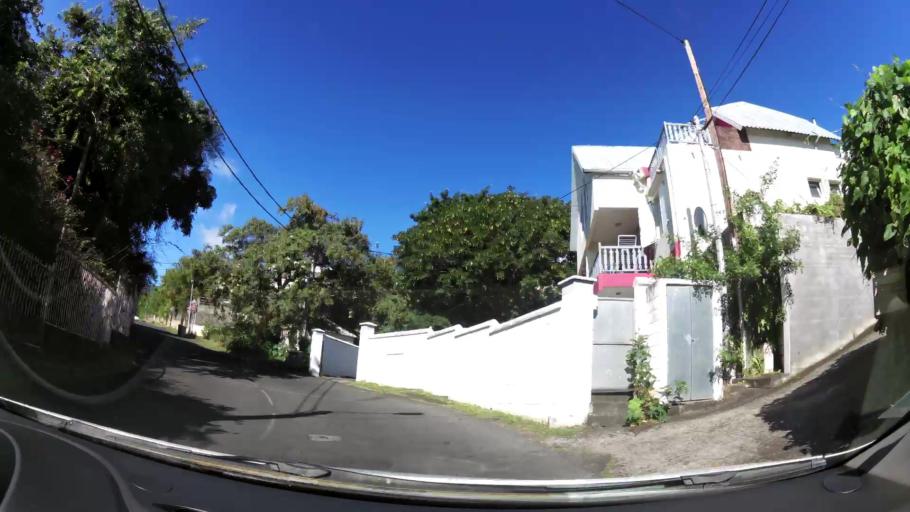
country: RE
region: Reunion
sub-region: Reunion
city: Saint-Denis
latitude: -20.9157
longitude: 55.4834
